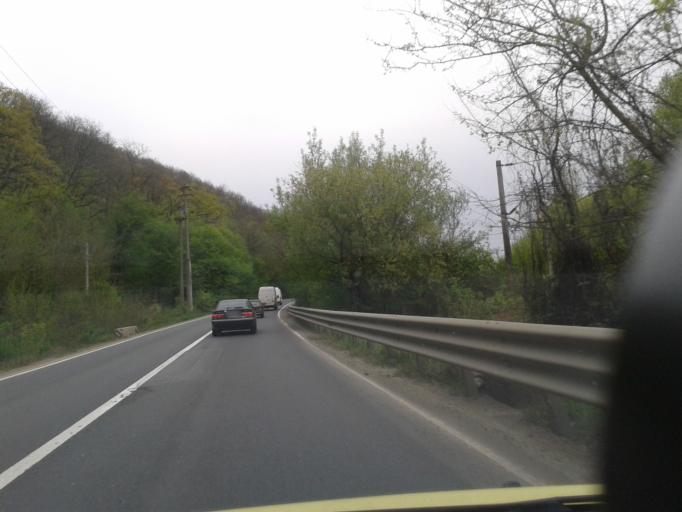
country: RO
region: Arad
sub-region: Comuna Bata
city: Bata
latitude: 46.0691
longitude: 22.0407
